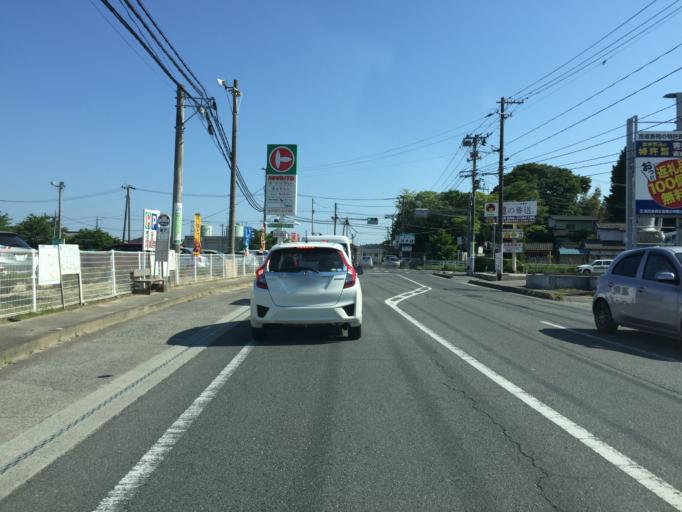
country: JP
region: Fukushima
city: Iwaki
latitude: 36.9908
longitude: 140.8540
